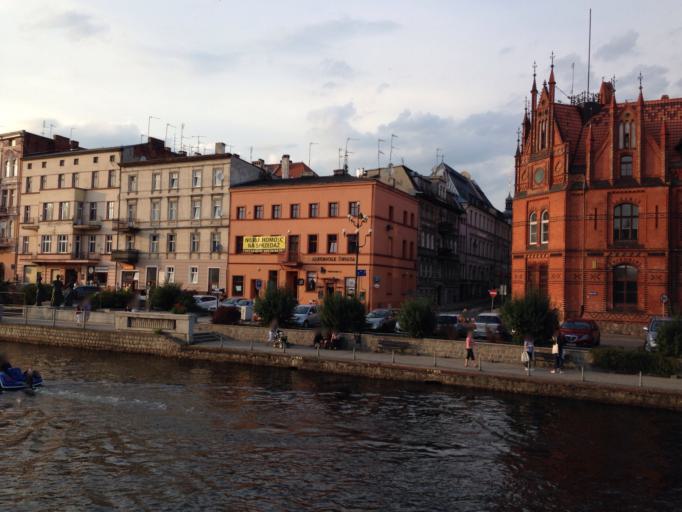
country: PL
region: Kujawsko-Pomorskie
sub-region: Bydgoszcz
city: Bydgoszcz
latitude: 53.1229
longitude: 18.0029
